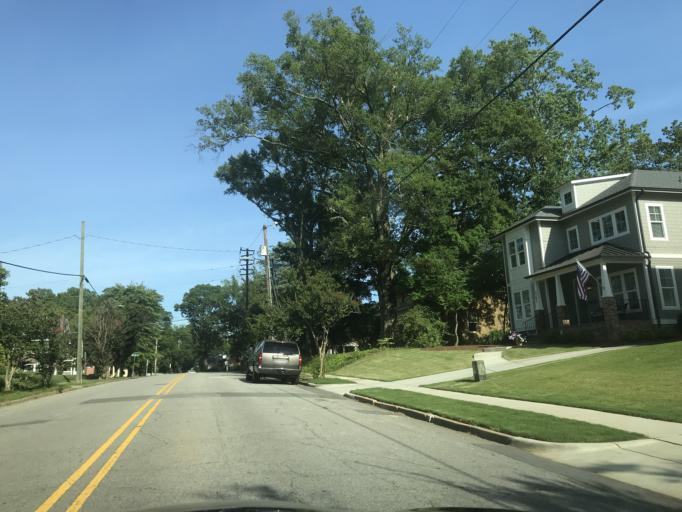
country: US
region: North Carolina
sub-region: Wake County
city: West Raleigh
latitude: 35.7931
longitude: -78.6788
